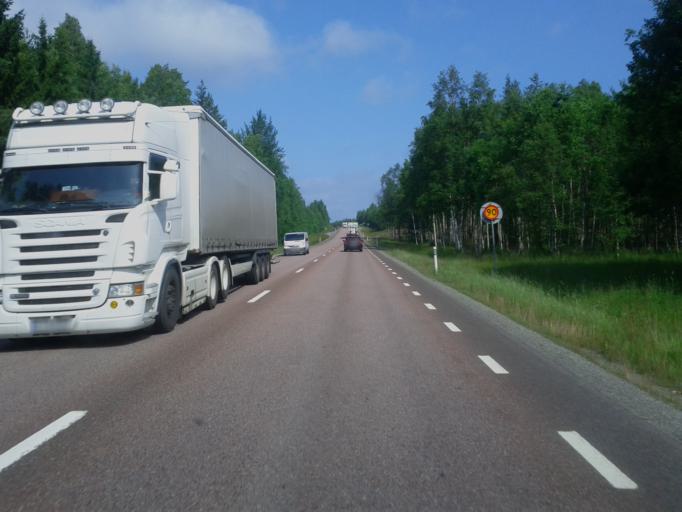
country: SE
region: Vaesterbotten
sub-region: Skelleftea Kommun
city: Burea
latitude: 64.6217
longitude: 21.1785
